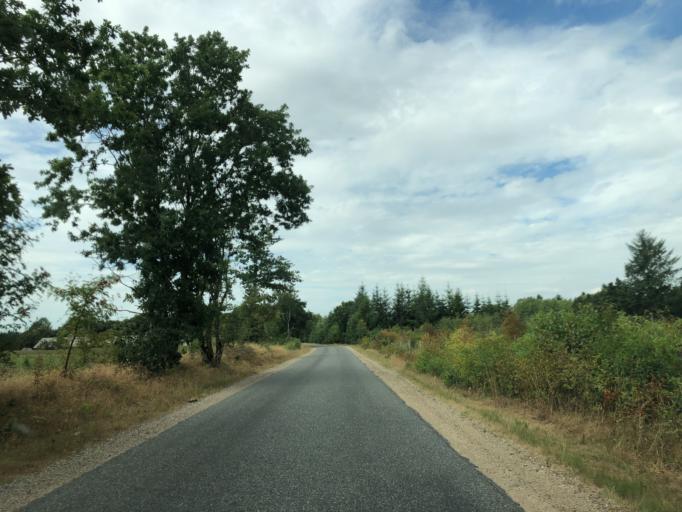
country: DK
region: South Denmark
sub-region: Billund Kommune
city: Grindsted
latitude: 55.6456
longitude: 8.9231
